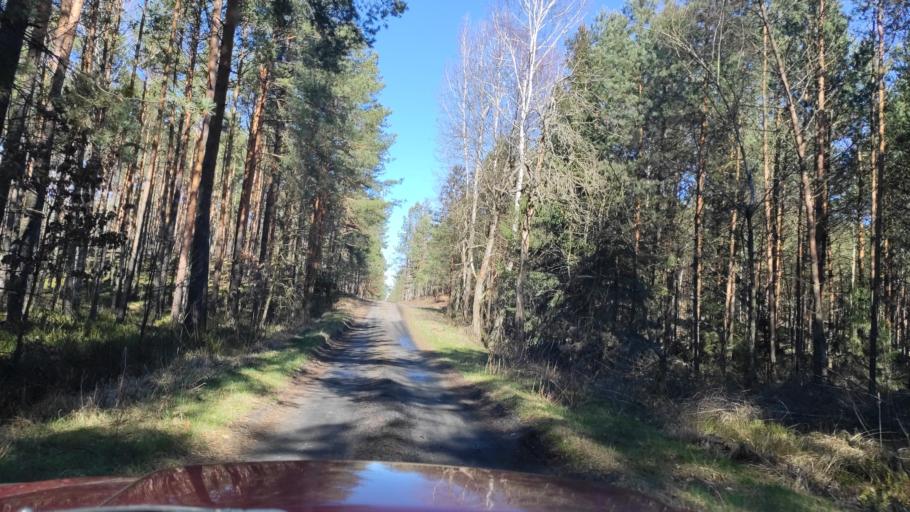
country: PL
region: Masovian Voivodeship
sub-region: Powiat zwolenski
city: Zwolen
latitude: 51.4113
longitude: 21.5564
